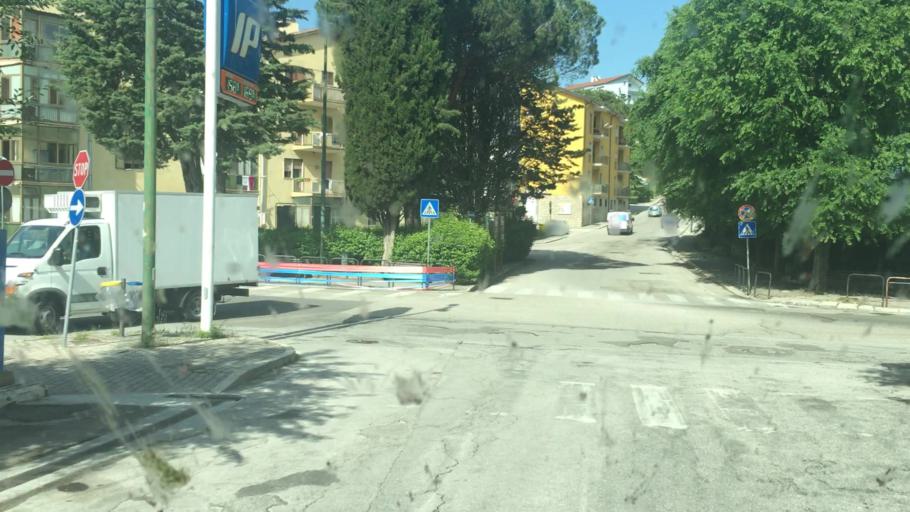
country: IT
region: Basilicate
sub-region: Provincia di Potenza
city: Potenza
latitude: 40.6443
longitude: 15.7984
